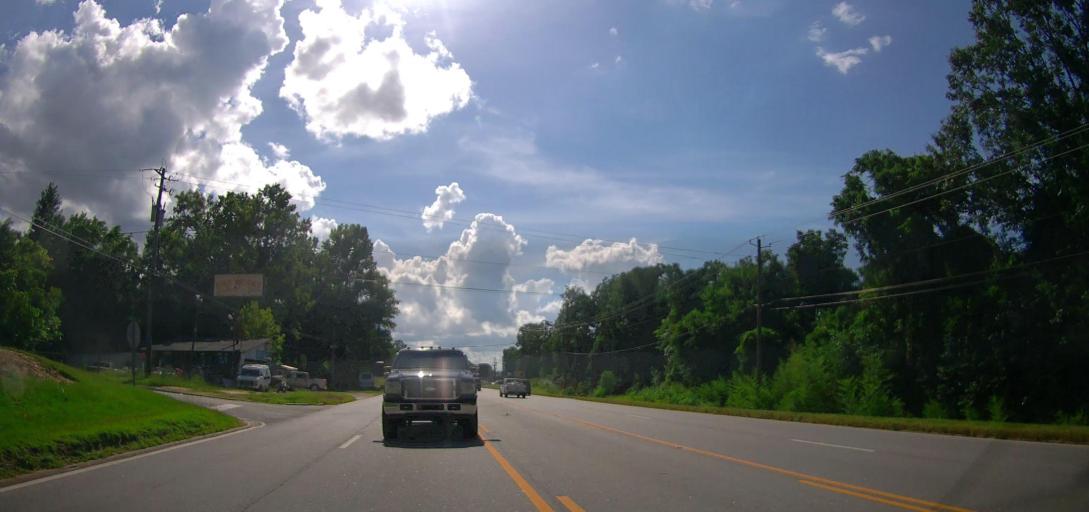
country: US
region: Alabama
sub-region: Russell County
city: Ladonia
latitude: 32.4679
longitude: -85.0737
